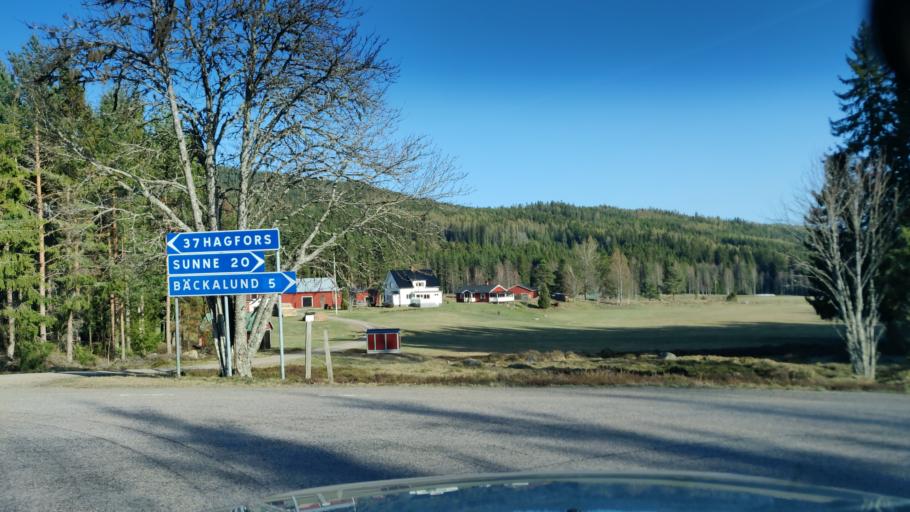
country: SE
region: Vaermland
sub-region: Sunne Kommun
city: Sunne
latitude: 59.9797
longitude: 13.2531
